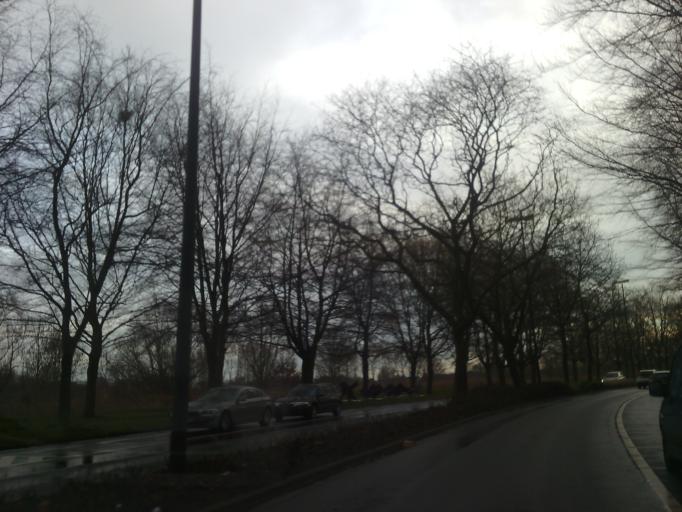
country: BE
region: Flanders
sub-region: Provincie Oost-Vlaanderen
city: Lokeren
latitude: 51.1082
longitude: 3.9949
